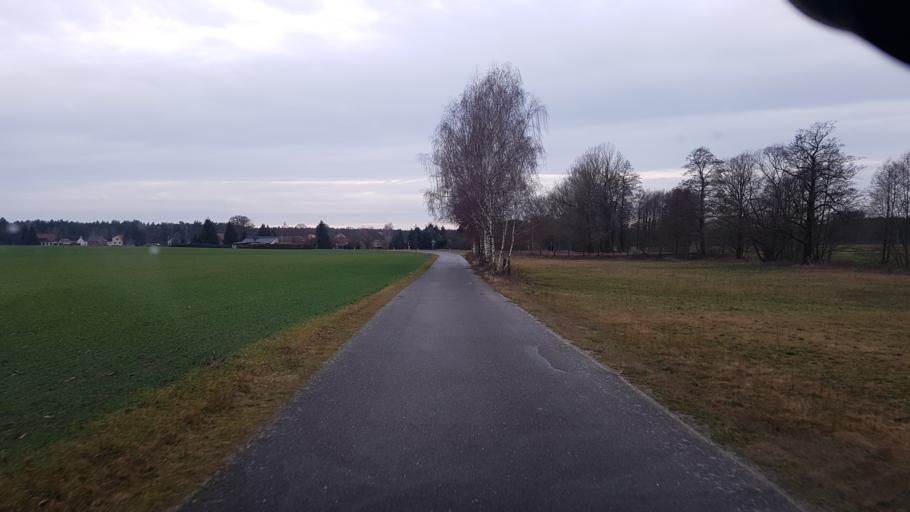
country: DE
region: Brandenburg
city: Crinitz
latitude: 51.6603
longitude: 13.7875
